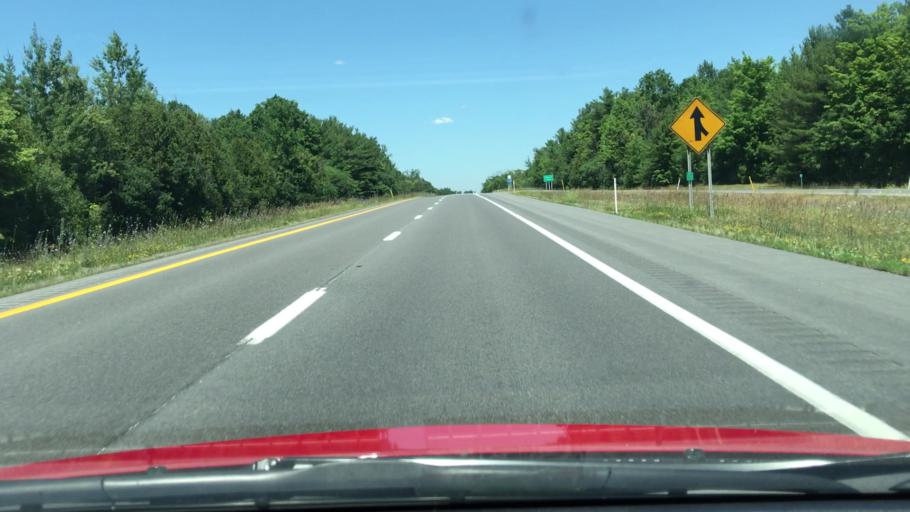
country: US
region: New York
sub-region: Clinton County
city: Cumberland Head
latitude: 44.8073
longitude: -73.4445
